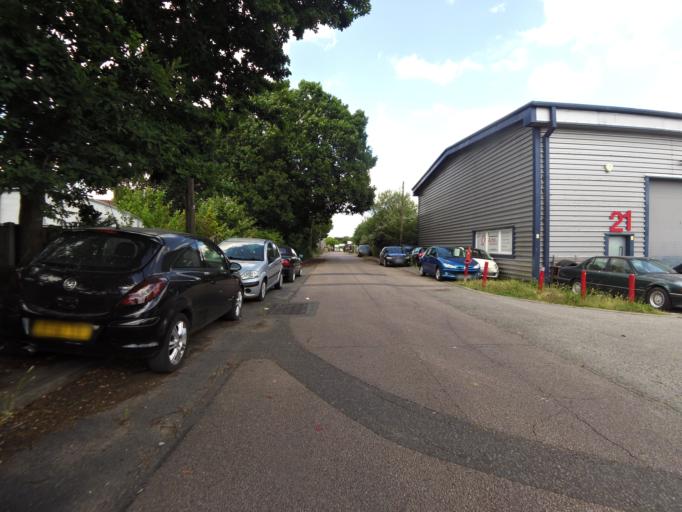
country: GB
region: England
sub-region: Suffolk
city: Kesgrave
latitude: 52.0364
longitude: 1.1991
